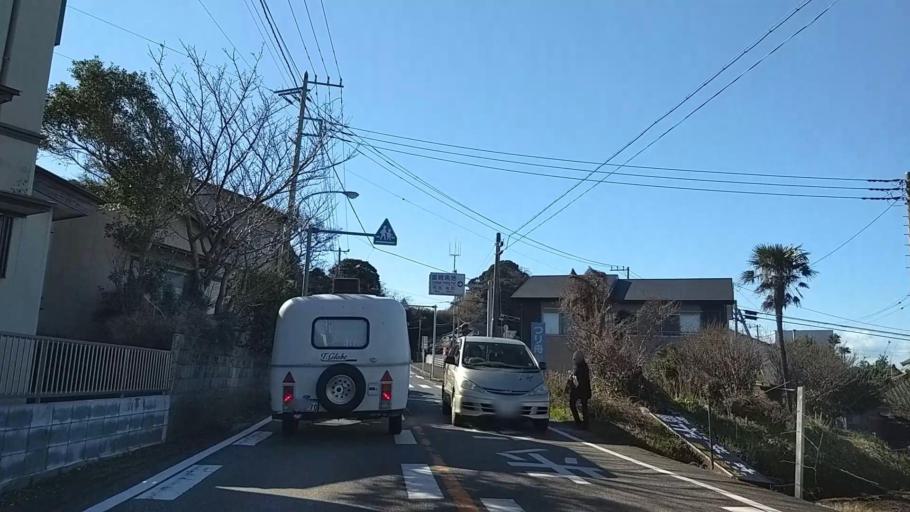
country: JP
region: Chiba
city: Tateyama
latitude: 34.9238
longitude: 139.8306
